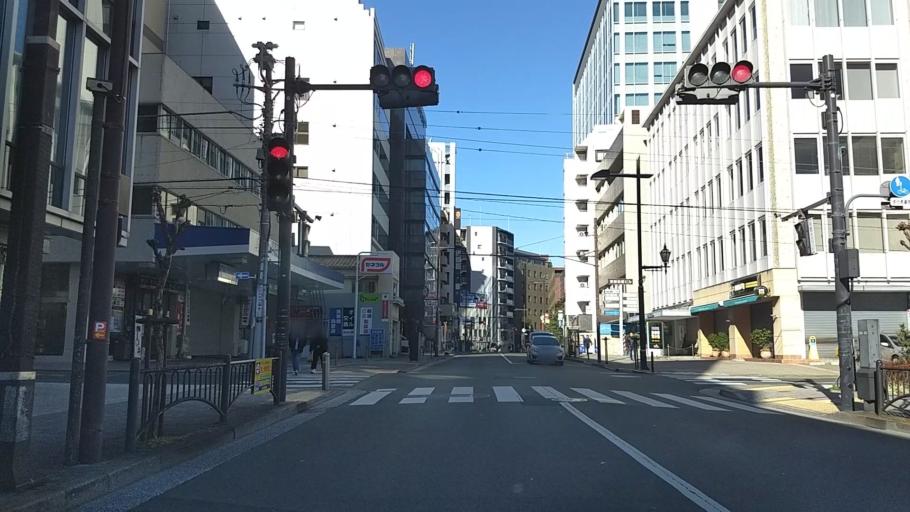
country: JP
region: Tokyo
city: Tokyo
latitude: 35.6881
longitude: 139.7358
